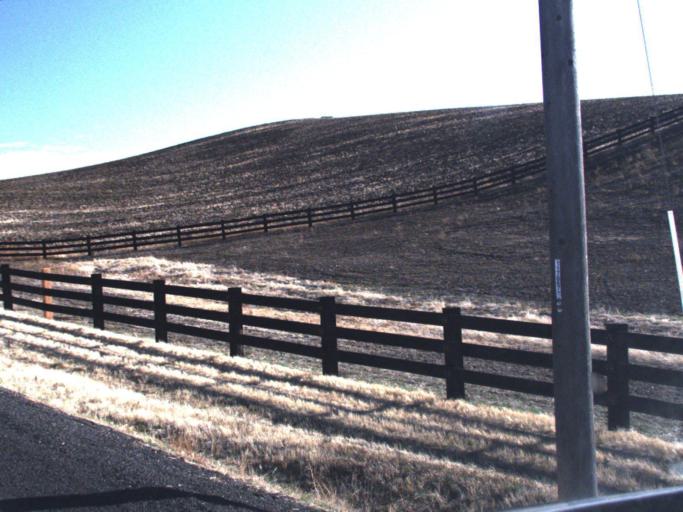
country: US
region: Washington
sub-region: Whitman County
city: Pullman
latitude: 46.7253
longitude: -117.2291
